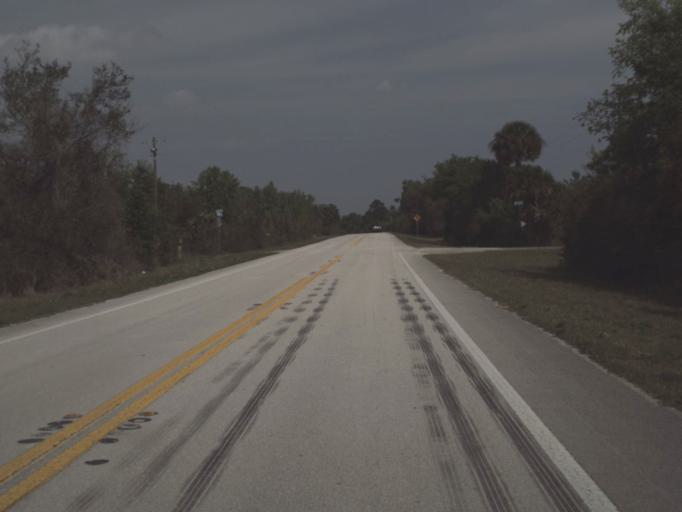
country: US
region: Florida
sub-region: Lake County
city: Astor
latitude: 29.2720
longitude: -81.6466
